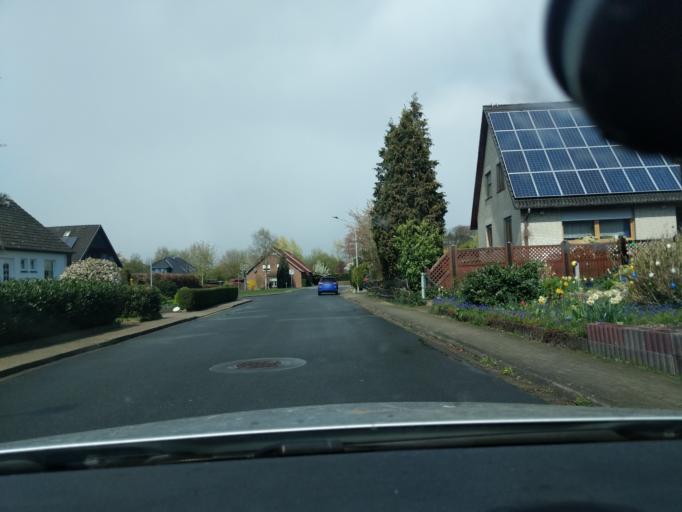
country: DE
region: Lower Saxony
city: Ahlerstedt
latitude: 53.4050
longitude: 9.4490
